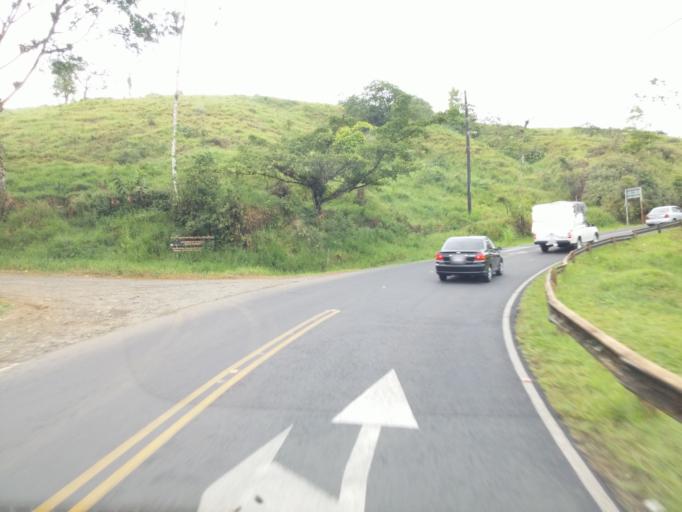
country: CR
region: Alajuela
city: Quesada
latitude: 10.2337
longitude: -84.5285
